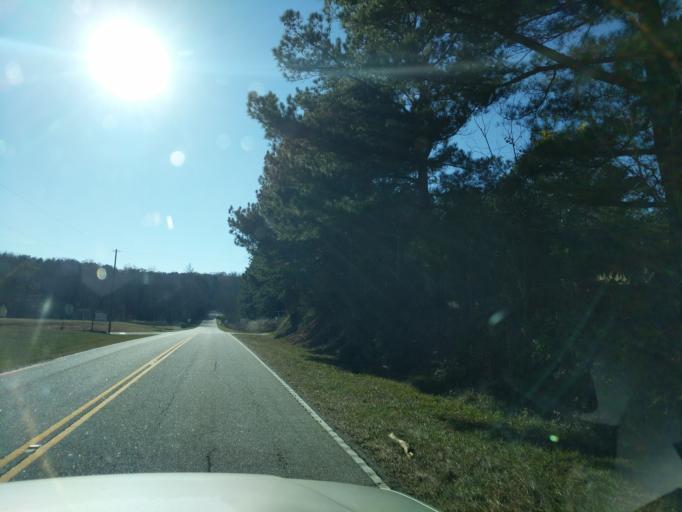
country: US
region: South Carolina
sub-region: Spartanburg County
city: Landrum
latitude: 35.1307
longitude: -82.1196
